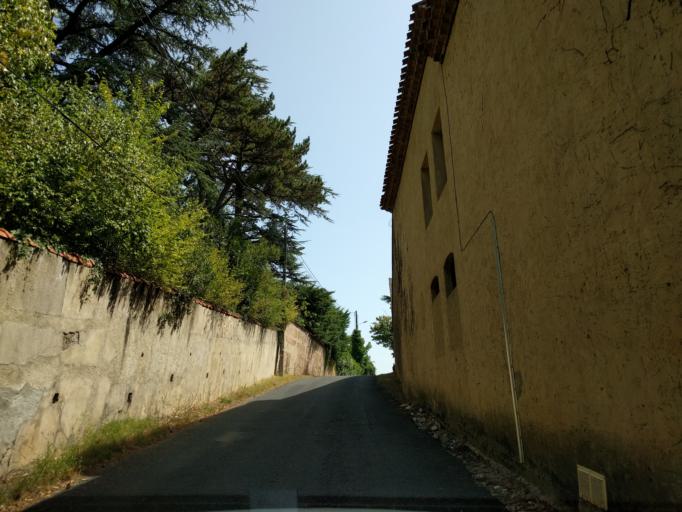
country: FR
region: Midi-Pyrenees
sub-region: Departement du Tarn
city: Castres
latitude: 43.5990
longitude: 2.2493
